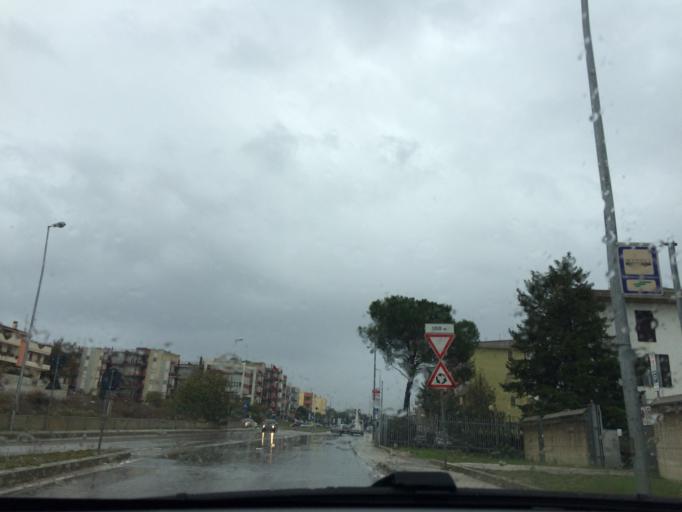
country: IT
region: Basilicate
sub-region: Provincia di Matera
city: Matera
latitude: 40.6819
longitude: 16.5794
